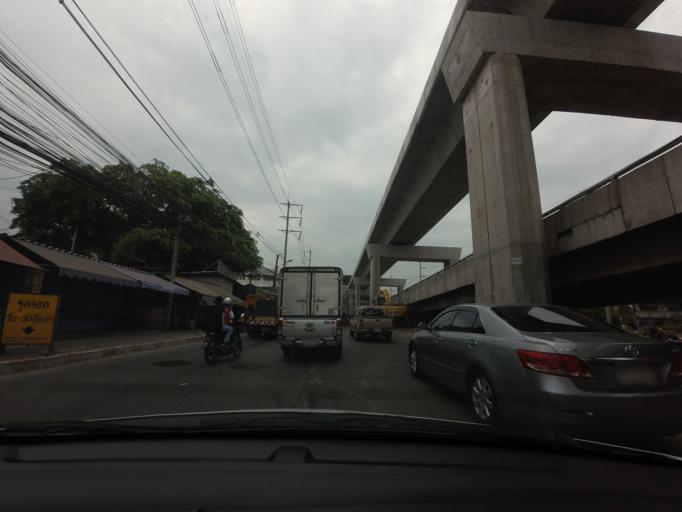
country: TH
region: Samut Prakan
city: Samut Prakan
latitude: 13.5939
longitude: 100.6081
